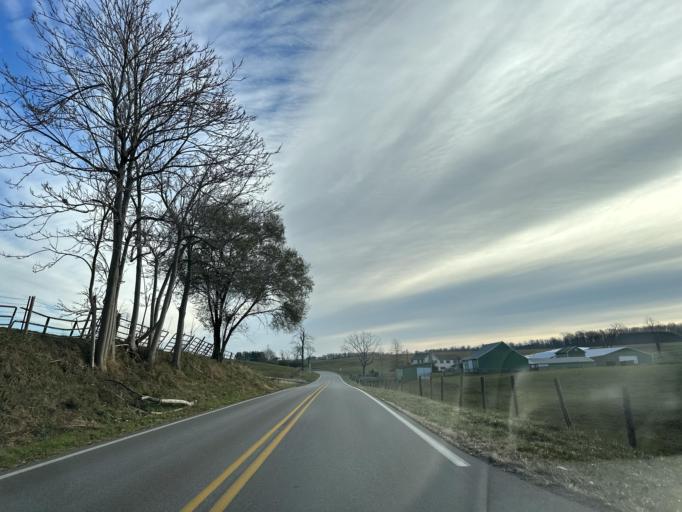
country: US
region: Virginia
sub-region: Rockingham County
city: Bridgewater
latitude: 38.3156
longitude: -79.0787
